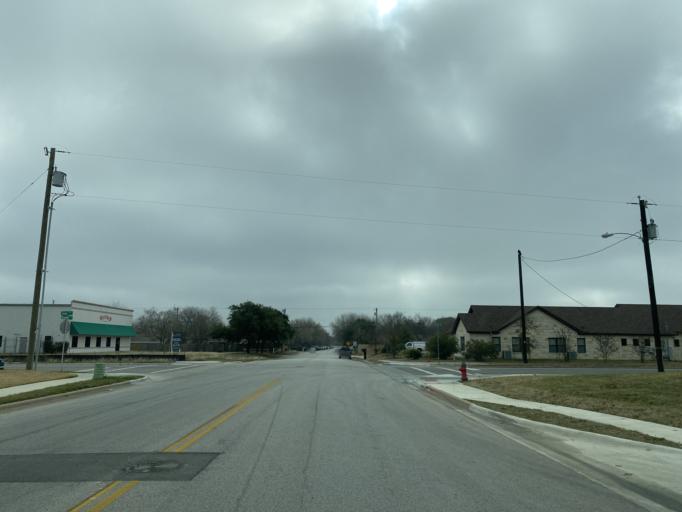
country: US
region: Texas
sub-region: Williamson County
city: Round Rock
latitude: 30.5316
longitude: -97.6807
